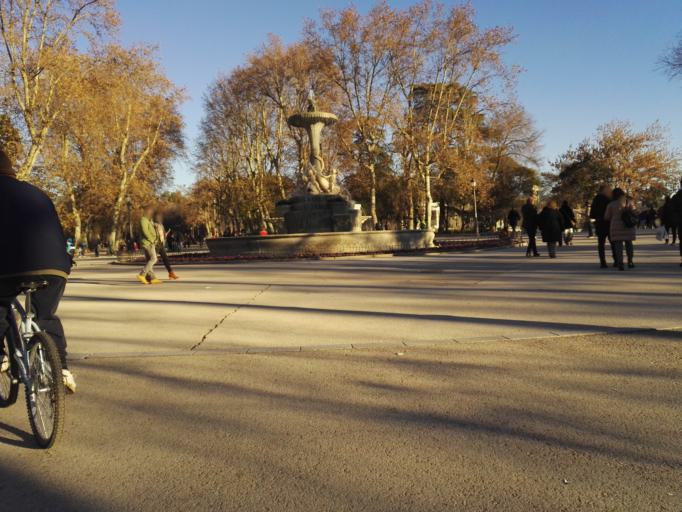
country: ES
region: Madrid
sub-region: Provincia de Madrid
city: Retiro
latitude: 40.4187
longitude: -3.6856
